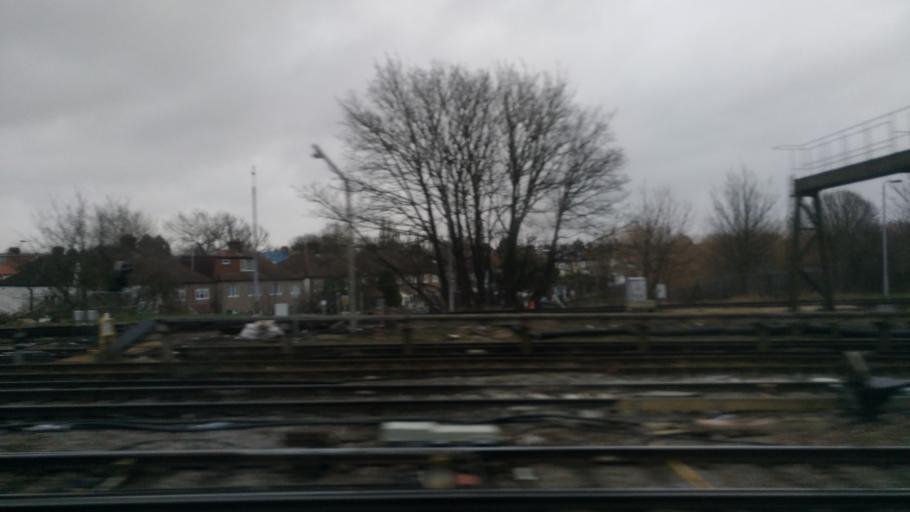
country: GB
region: England
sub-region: Greater London
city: Blackheath
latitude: 51.4448
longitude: 0.0062
